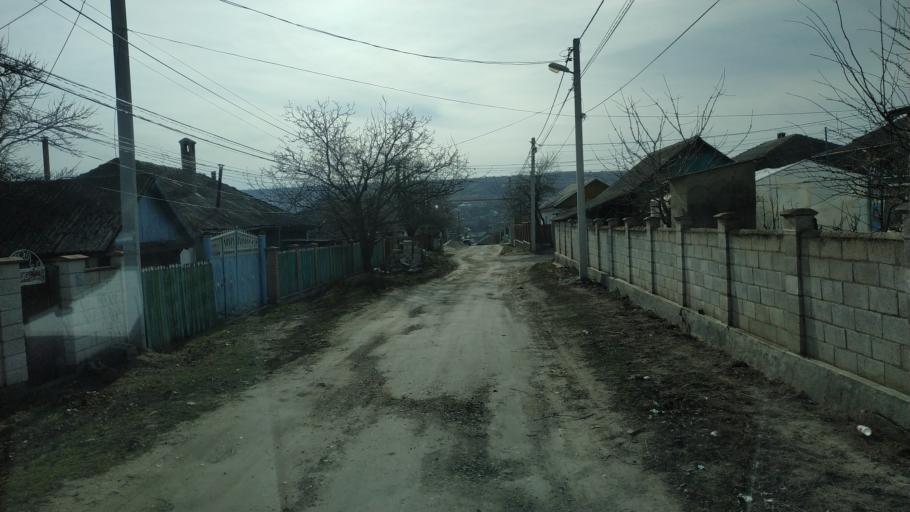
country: MD
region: Chisinau
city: Vatra
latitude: 47.0762
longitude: 28.6849
